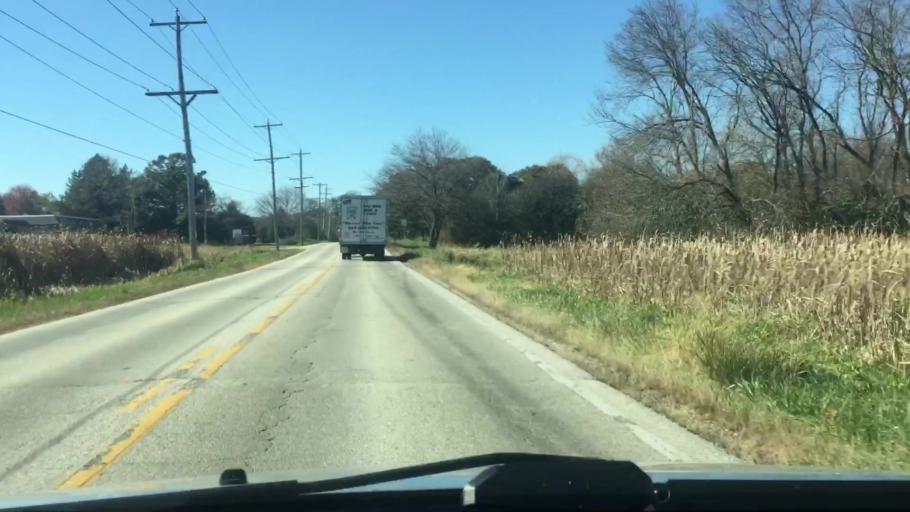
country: US
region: Wisconsin
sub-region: Waukesha County
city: Wales
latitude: 42.9880
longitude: -88.3220
